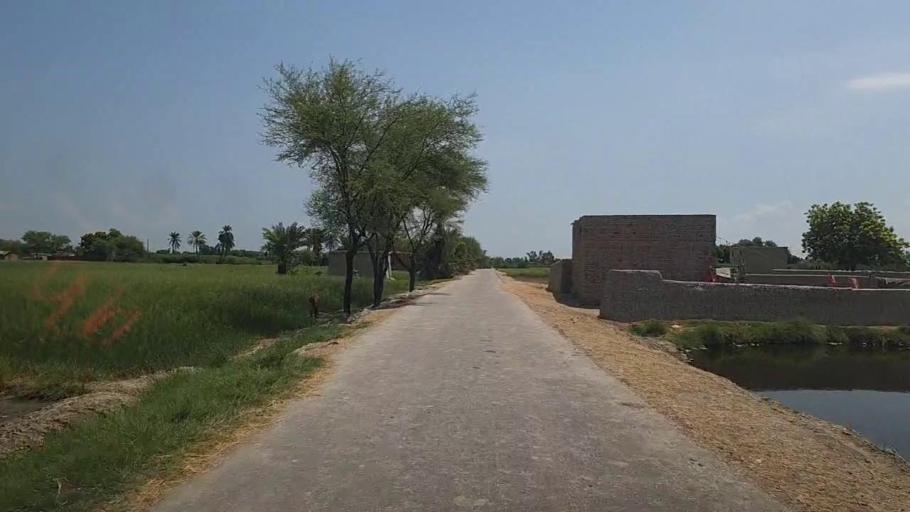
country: PK
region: Sindh
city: Ubauro
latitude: 28.1530
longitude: 69.7667
